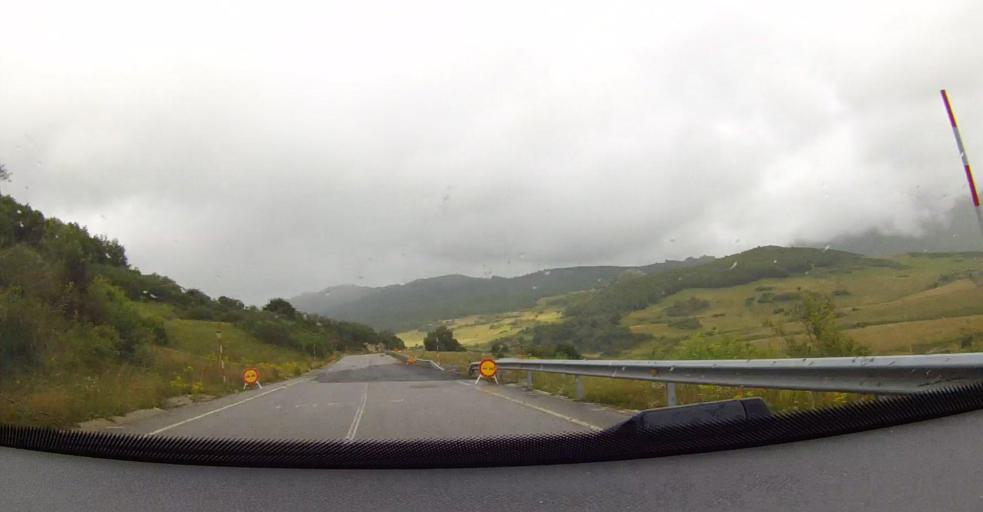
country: ES
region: Castille and Leon
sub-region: Provincia de Leon
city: Marana
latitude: 43.0722
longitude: -5.2042
